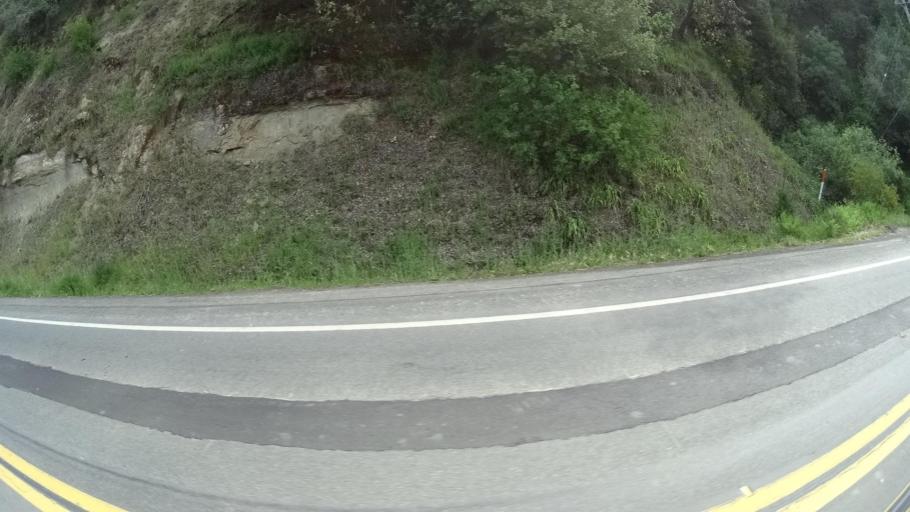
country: US
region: California
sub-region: Humboldt County
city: Redway
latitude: 40.1148
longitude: -123.7950
